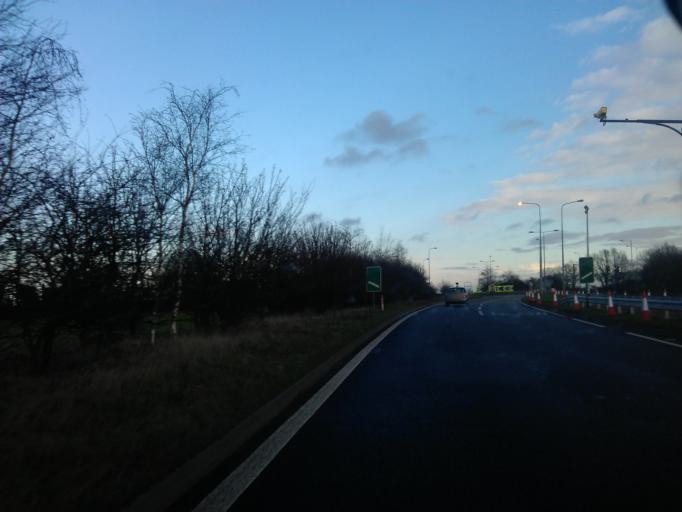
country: GB
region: England
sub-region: Essex
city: Mistley
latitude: 51.9040
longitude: 1.0838
